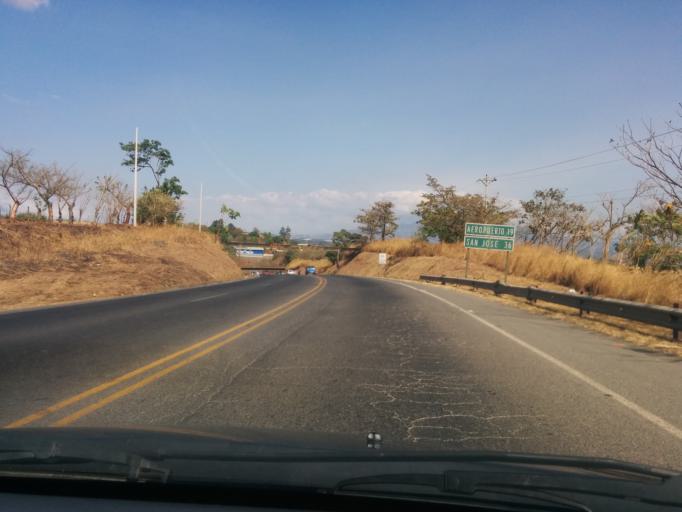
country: CR
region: Alajuela
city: Atenas
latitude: 10.0168
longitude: -84.3549
